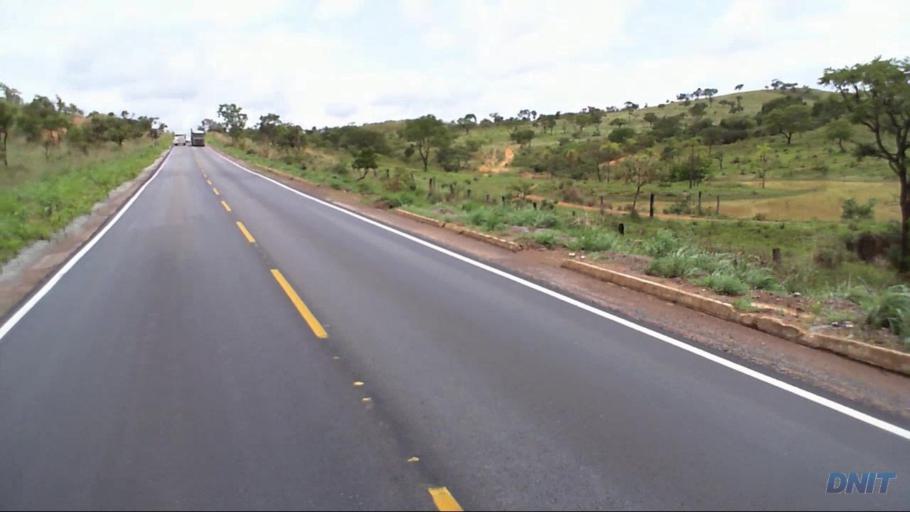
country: BR
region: Goias
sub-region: Padre Bernardo
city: Padre Bernardo
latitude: -15.4732
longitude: -48.2307
